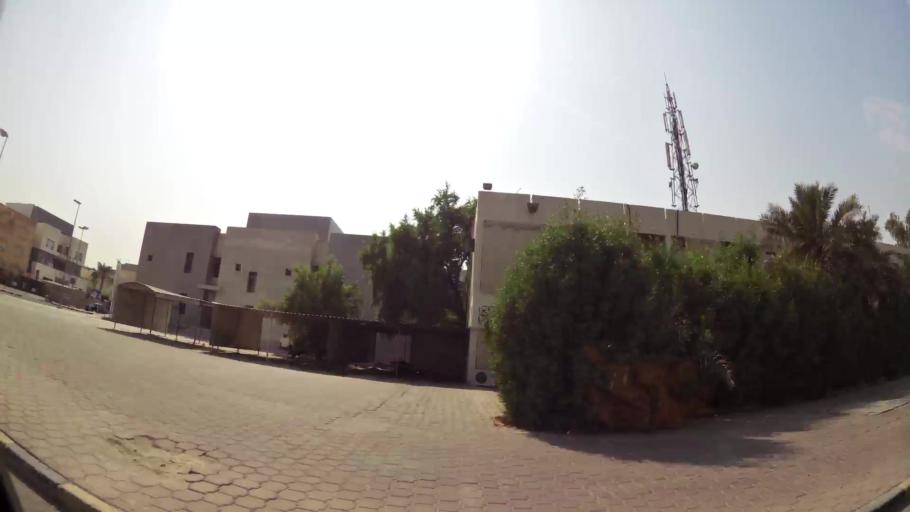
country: KW
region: Muhafazat Hawalli
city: Hawalli
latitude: 29.3489
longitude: 48.0268
